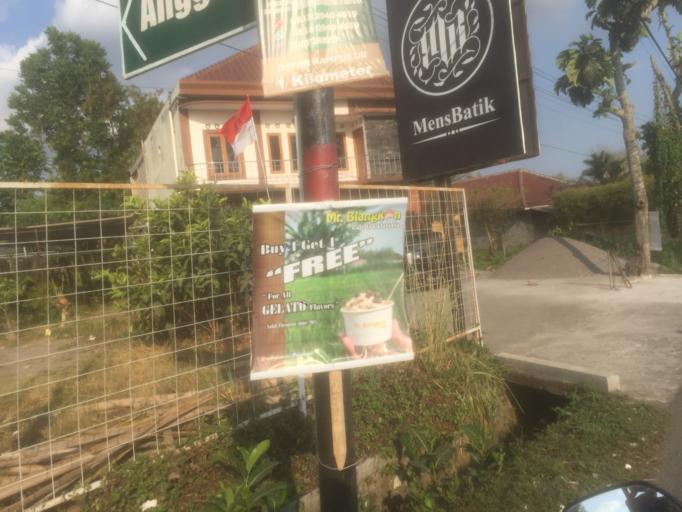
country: ID
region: Daerah Istimewa Yogyakarta
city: Sleman
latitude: -7.6791
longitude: 110.4179
